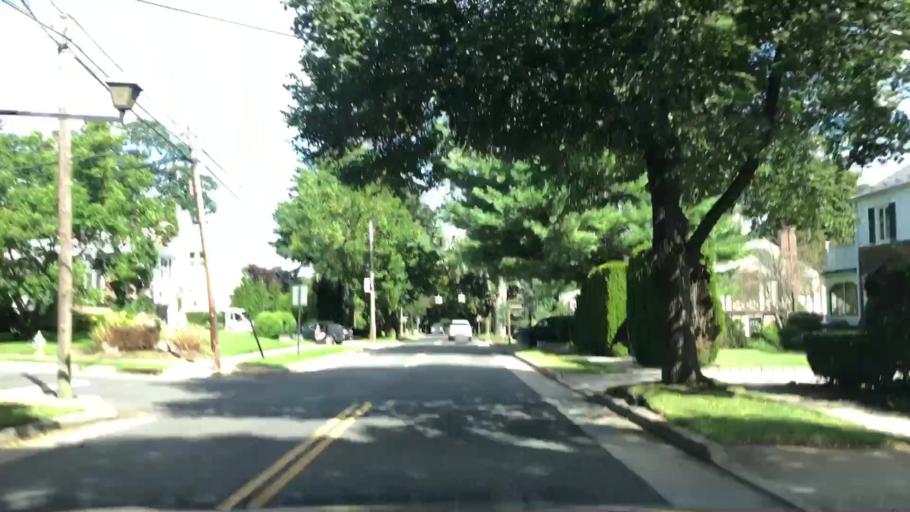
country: US
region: New York
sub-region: Nassau County
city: Manhasset
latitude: 40.7948
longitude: -73.6953
